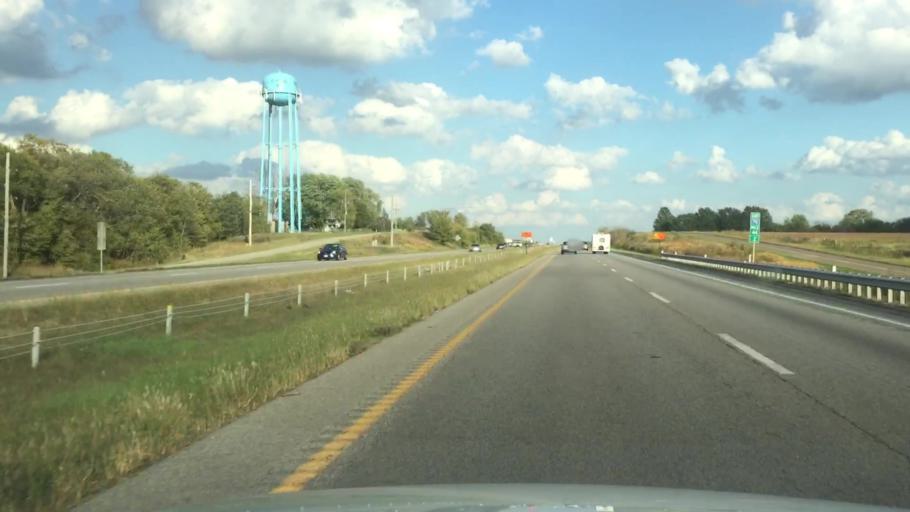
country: US
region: Missouri
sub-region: Lafayette County
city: Odessa
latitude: 39.0033
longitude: -93.8286
